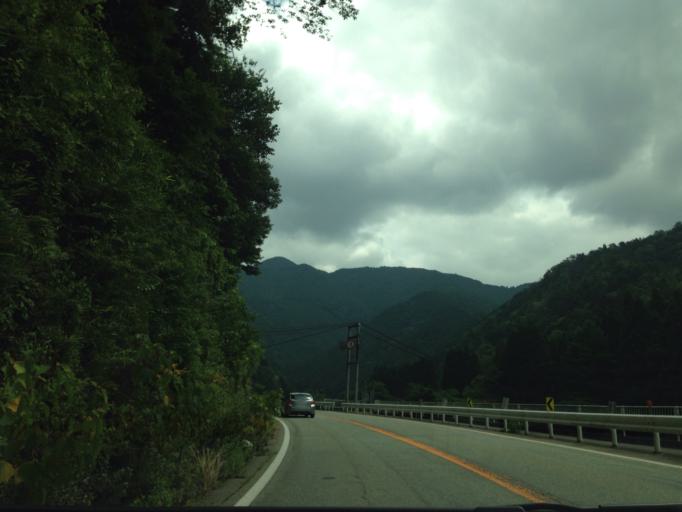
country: JP
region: Gifu
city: Gujo
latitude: 35.7489
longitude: 137.2175
